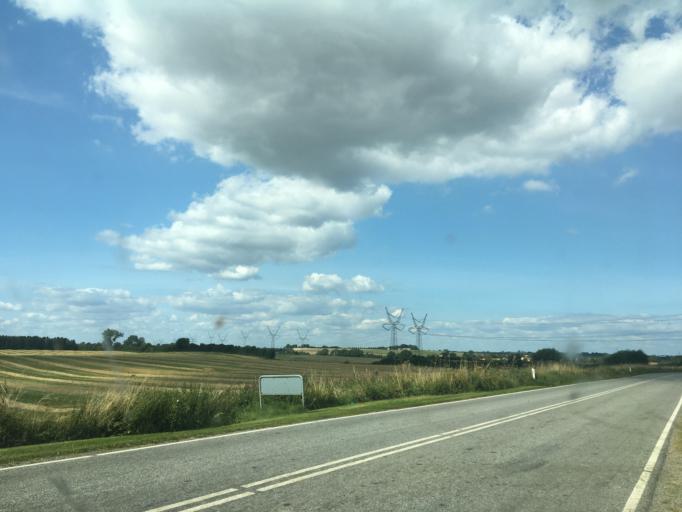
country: DK
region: South Denmark
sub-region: Middelfart Kommune
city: Ejby
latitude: 55.4160
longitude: 9.9195
